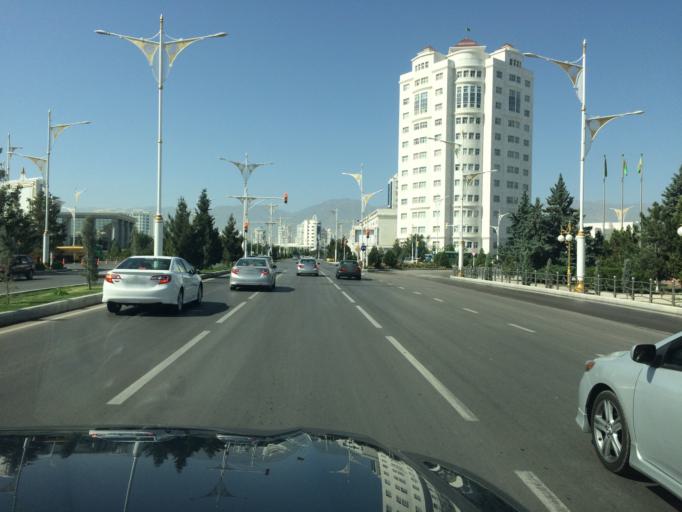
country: TM
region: Ahal
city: Ashgabat
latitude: 37.9169
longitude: 58.3721
